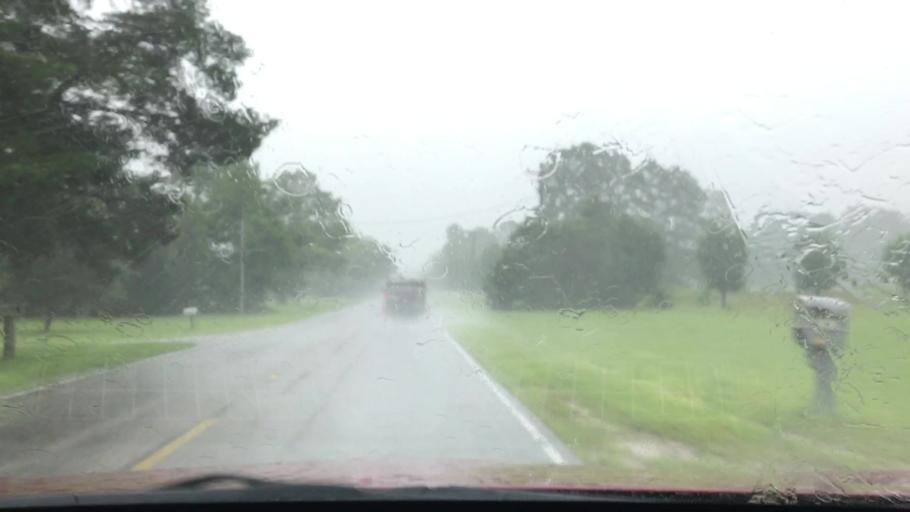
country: US
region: South Carolina
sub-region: Horry County
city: Red Hill
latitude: 33.8974
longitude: -78.9321
